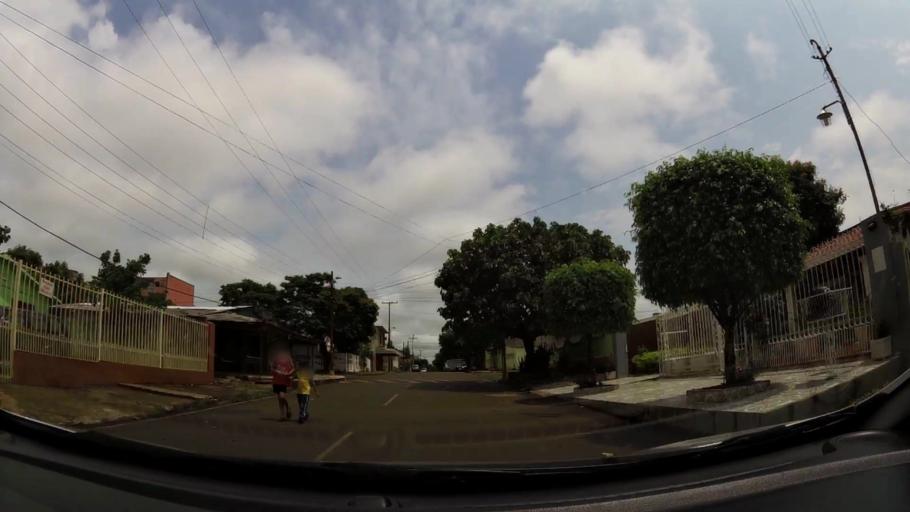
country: PY
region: Alto Parana
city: Ciudad del Este
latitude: -25.5044
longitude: -54.6580
